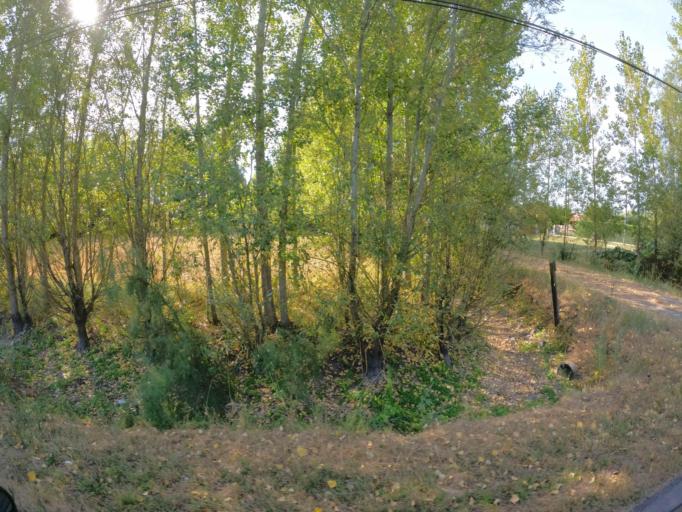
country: FR
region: Pays de la Loire
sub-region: Departement de la Vendee
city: Le Perrier
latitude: 46.8054
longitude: -1.9793
